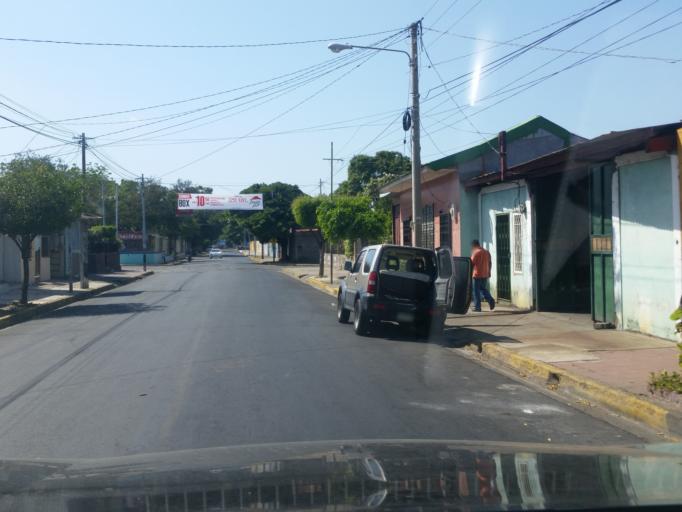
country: NI
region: Managua
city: Managua
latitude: 12.1484
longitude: -86.2953
